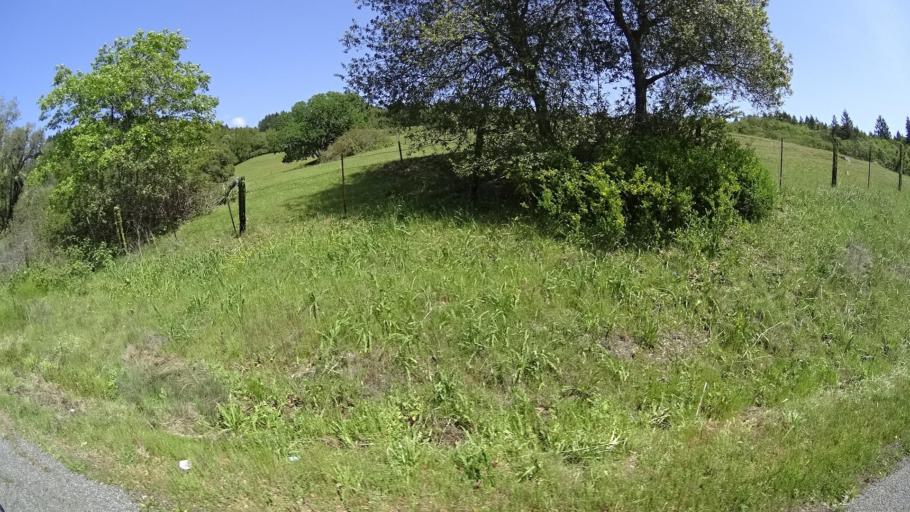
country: US
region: California
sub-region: Humboldt County
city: Redway
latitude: 40.2534
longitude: -123.6241
